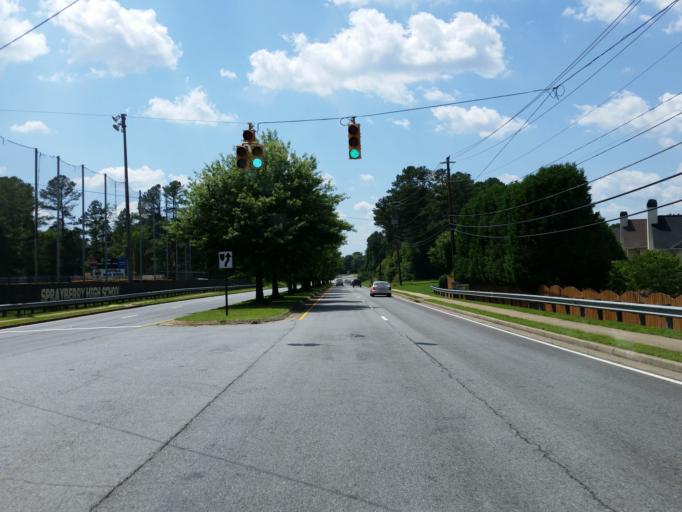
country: US
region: Georgia
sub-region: Cobb County
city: Marietta
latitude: 34.0139
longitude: -84.4986
